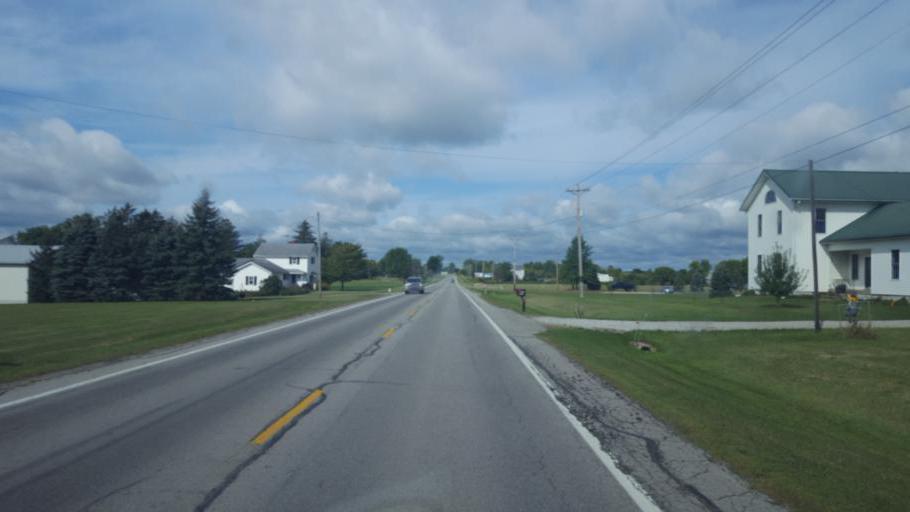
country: US
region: Ohio
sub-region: Lorain County
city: Wellington
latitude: 41.1689
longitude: -82.1557
